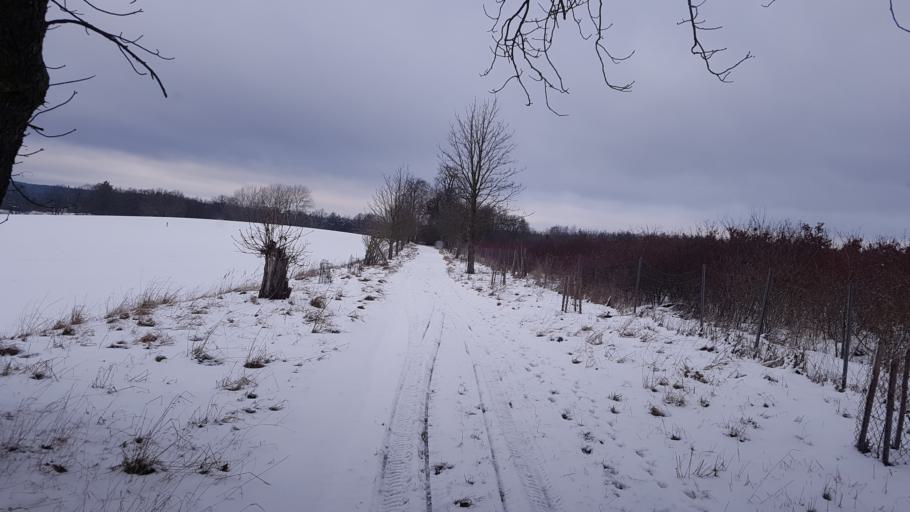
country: DE
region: Brandenburg
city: Crinitz
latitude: 51.7312
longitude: 13.7687
